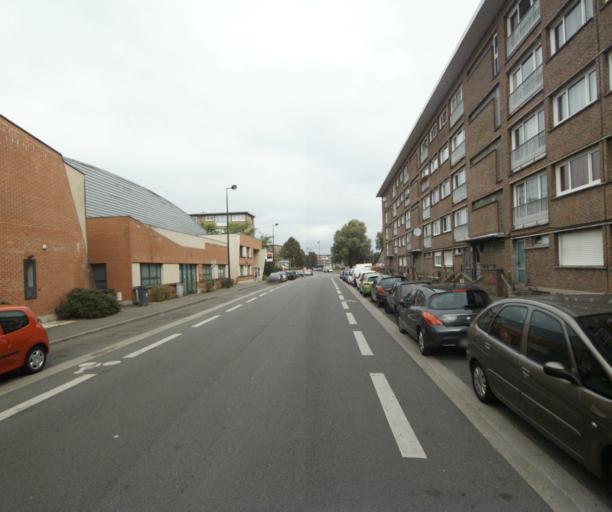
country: FR
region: Nord-Pas-de-Calais
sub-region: Departement du Nord
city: Lannoy
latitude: 50.6759
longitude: 3.1948
